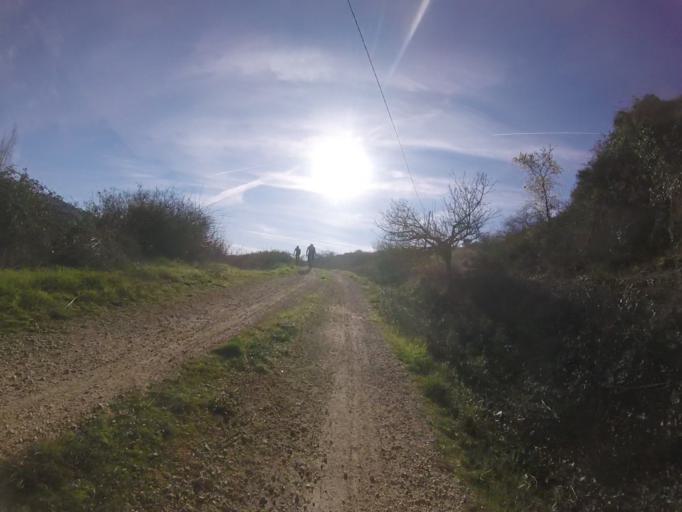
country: ES
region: Navarre
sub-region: Provincia de Navarra
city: Yerri
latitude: 42.6868
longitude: -1.9592
